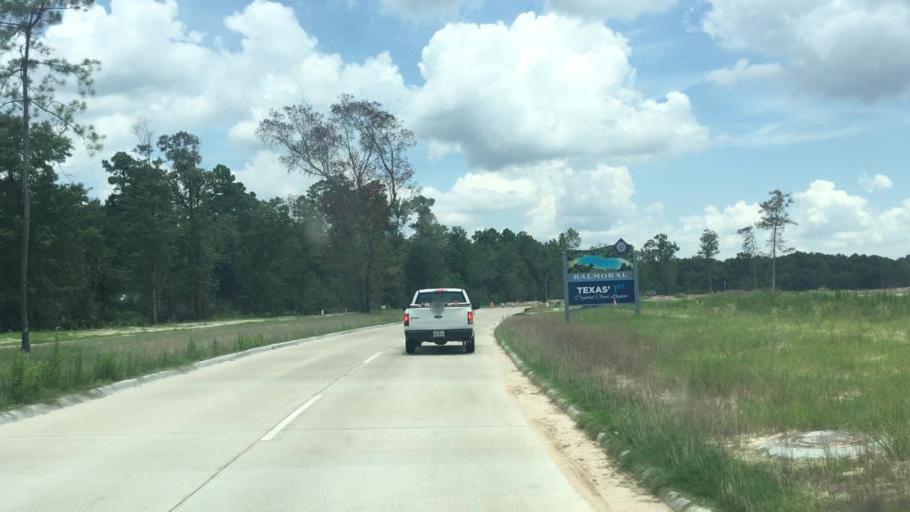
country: US
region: Texas
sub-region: Harris County
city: Atascocita
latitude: 29.9495
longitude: -95.2109
